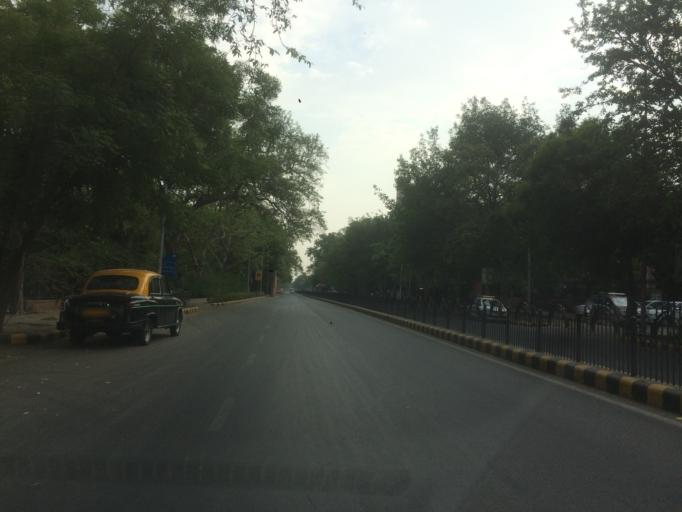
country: IN
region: NCT
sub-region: New Delhi
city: New Delhi
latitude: 28.6213
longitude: 77.2189
